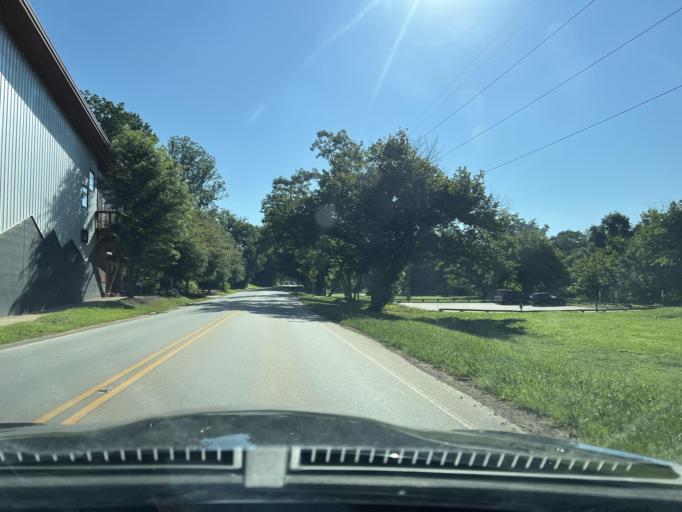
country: US
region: North Carolina
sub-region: Buncombe County
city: Asheville
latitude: 35.5674
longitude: -82.5699
